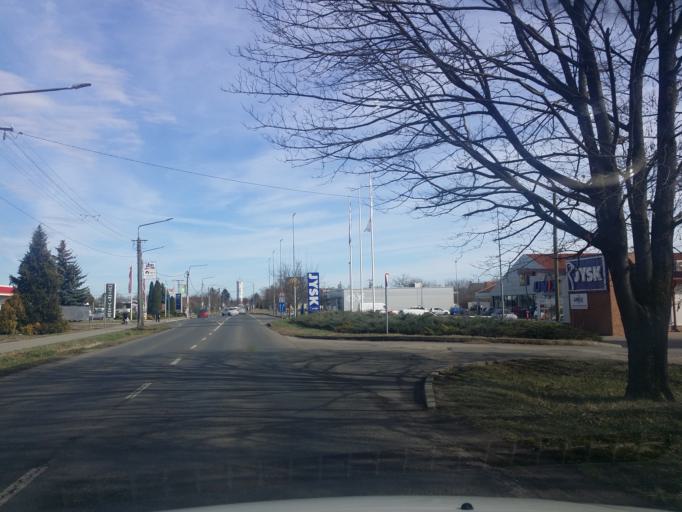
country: HU
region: Baranya
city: Mohacs
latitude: 45.9969
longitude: 18.6672
